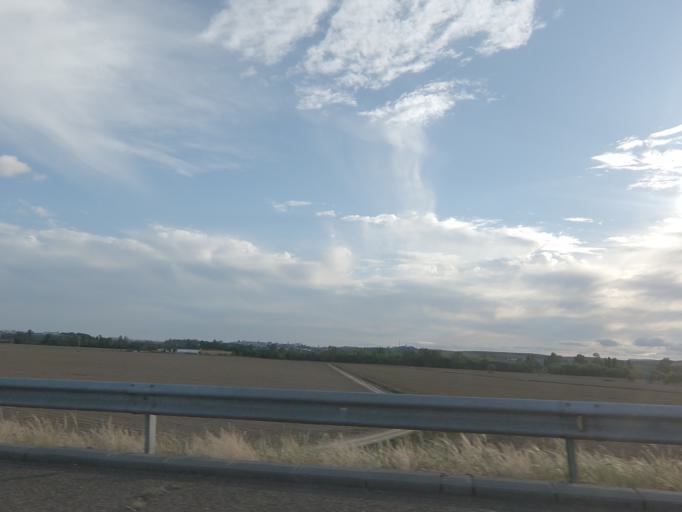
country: ES
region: Extremadura
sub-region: Provincia de Badajoz
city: Badajoz
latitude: 38.9149
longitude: -6.9511
